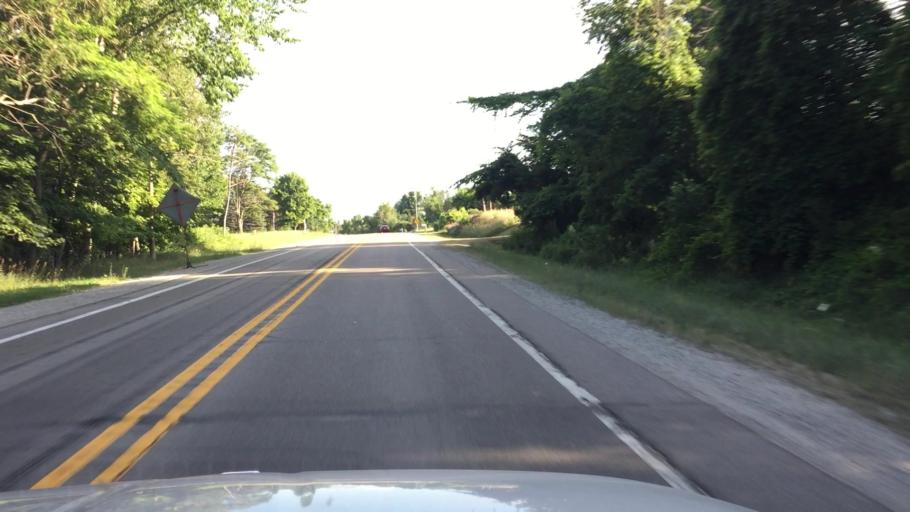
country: US
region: Michigan
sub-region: Saint Clair County
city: Yale
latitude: 43.0696
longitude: -82.7662
